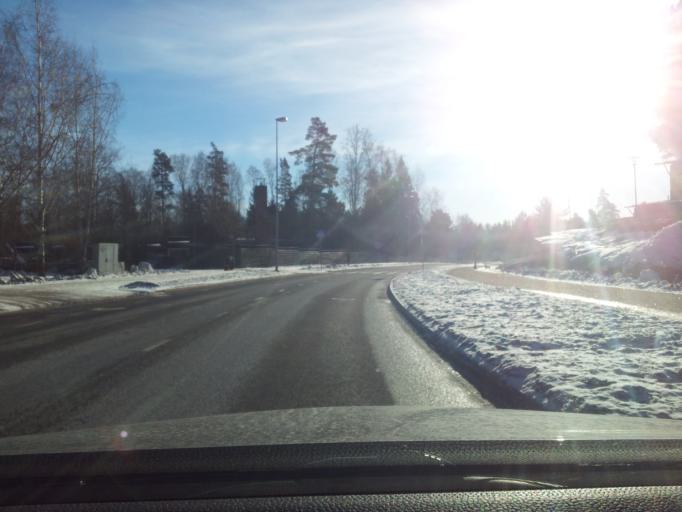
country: FI
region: Uusimaa
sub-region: Helsinki
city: Koukkuniemi
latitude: 60.1510
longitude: 24.7363
